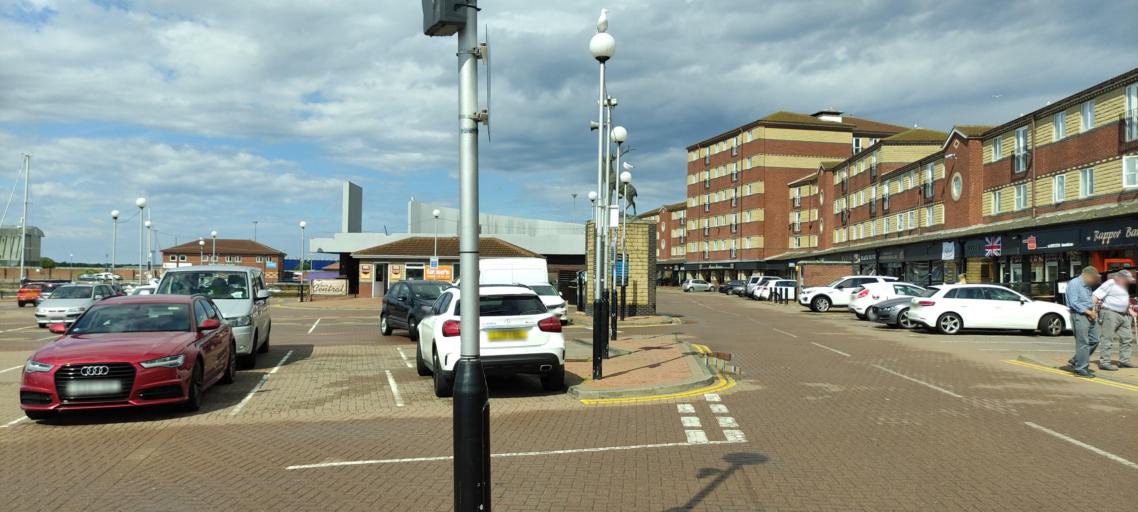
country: GB
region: England
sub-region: Hartlepool
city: Hartlepool
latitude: 54.6915
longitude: -1.1989
